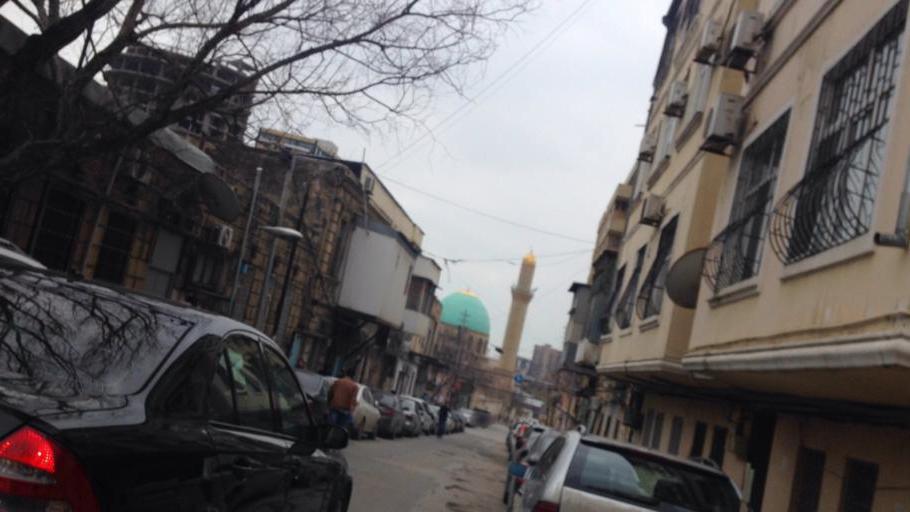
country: AZ
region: Baki
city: Badamdar
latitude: 40.3804
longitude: 49.8287
